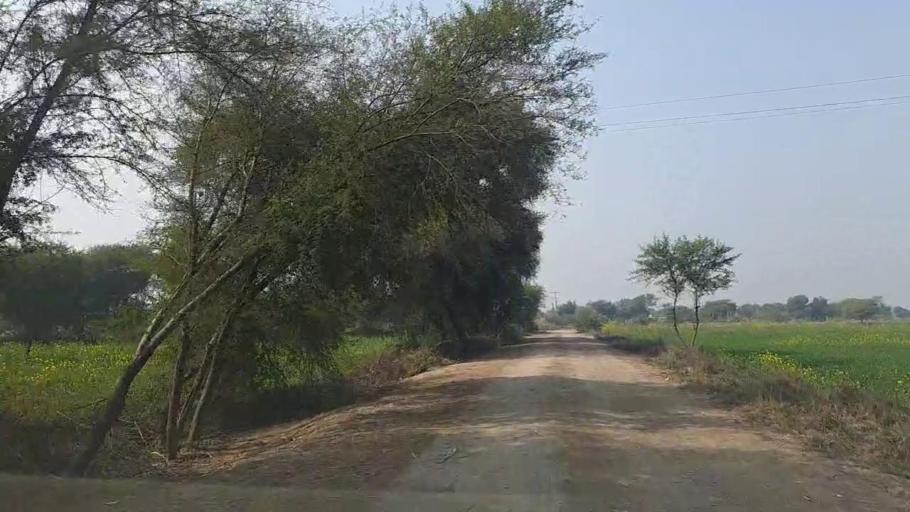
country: PK
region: Sindh
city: Daur
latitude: 26.4198
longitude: 68.4473
